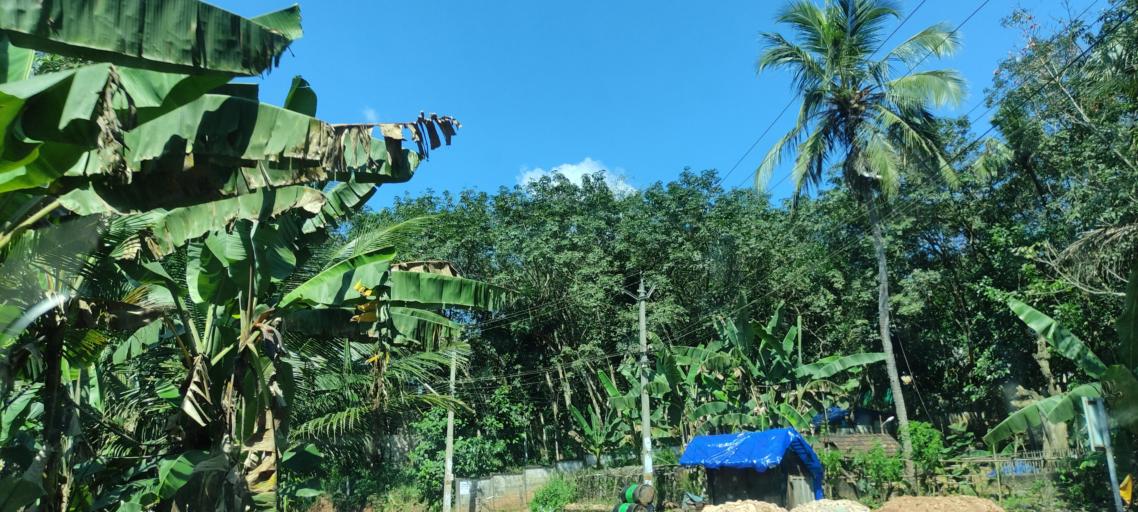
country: IN
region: Kerala
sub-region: Pattanamtitta
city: Adur
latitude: 9.1103
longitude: 76.7289
